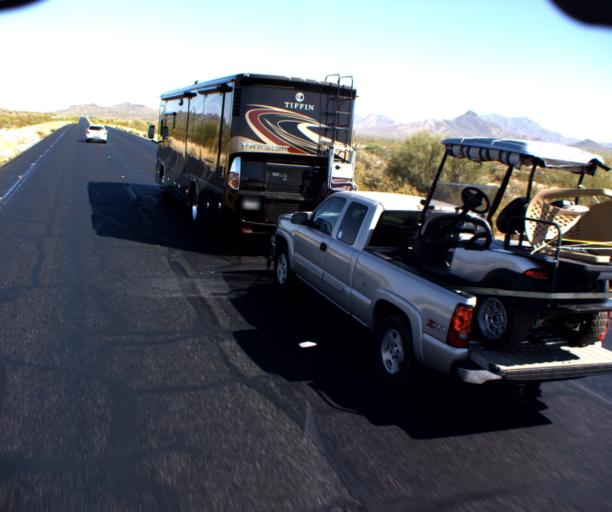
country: US
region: Arizona
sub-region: Pinal County
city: Maricopa
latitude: 32.8384
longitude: -112.2256
